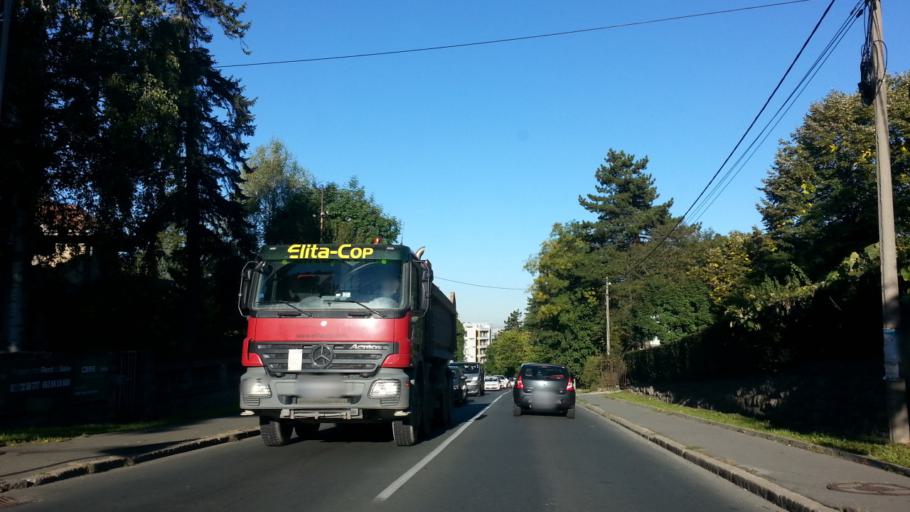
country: RS
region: Central Serbia
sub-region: Belgrade
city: Savski Venac
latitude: 44.7795
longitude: 20.4544
